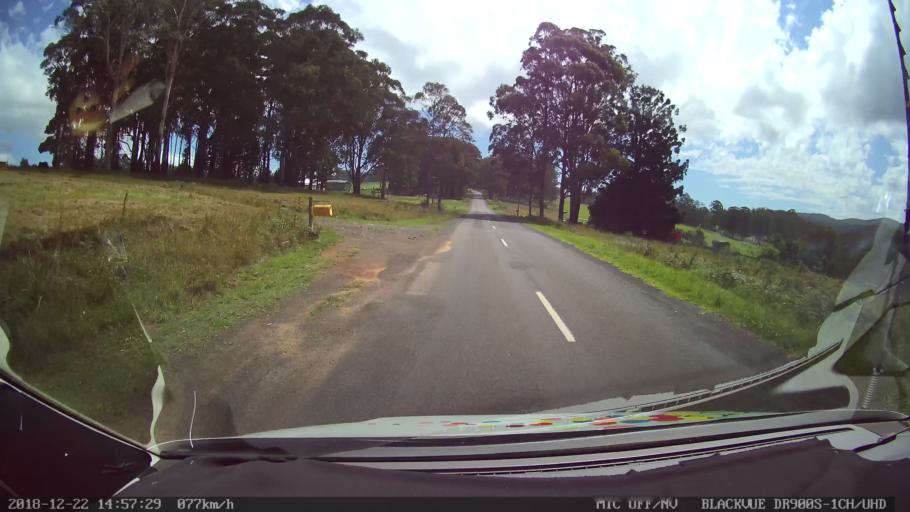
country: AU
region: New South Wales
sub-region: Bellingen
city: Dorrigo
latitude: -30.2346
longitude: 152.5007
